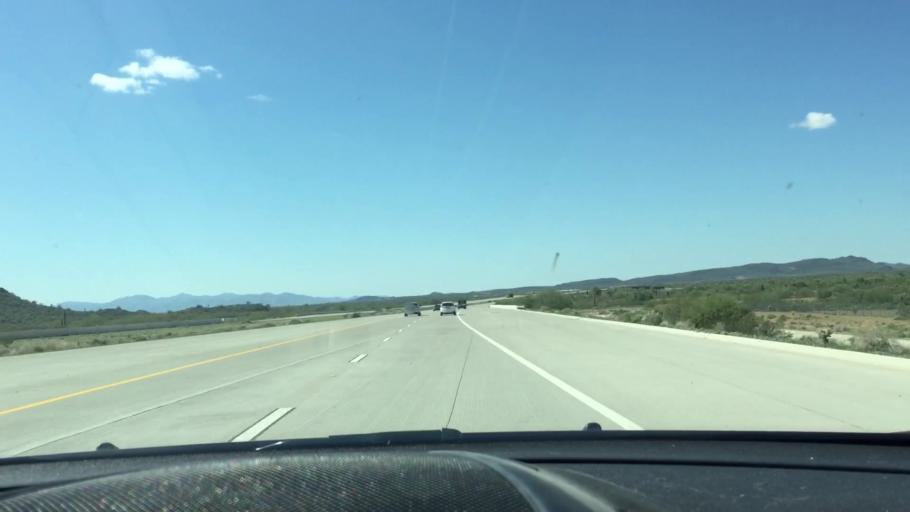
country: US
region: Arizona
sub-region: Maricopa County
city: Anthem
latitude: 33.7807
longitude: -112.2099
